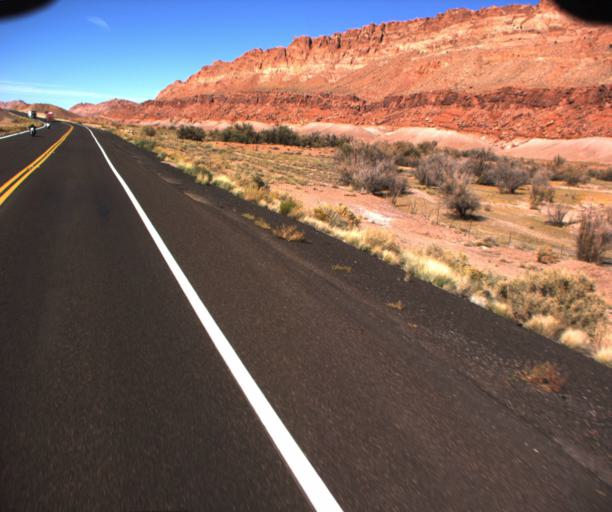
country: US
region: Arizona
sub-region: Coconino County
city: Tuba City
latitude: 36.2241
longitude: -111.3997
